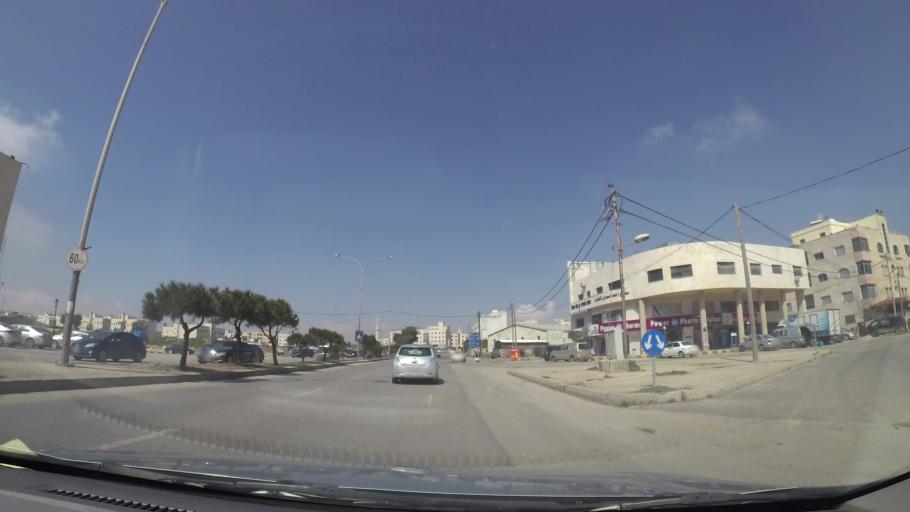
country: JO
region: Amman
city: Al Bunayyat ash Shamaliyah
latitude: 31.9047
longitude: 35.8877
